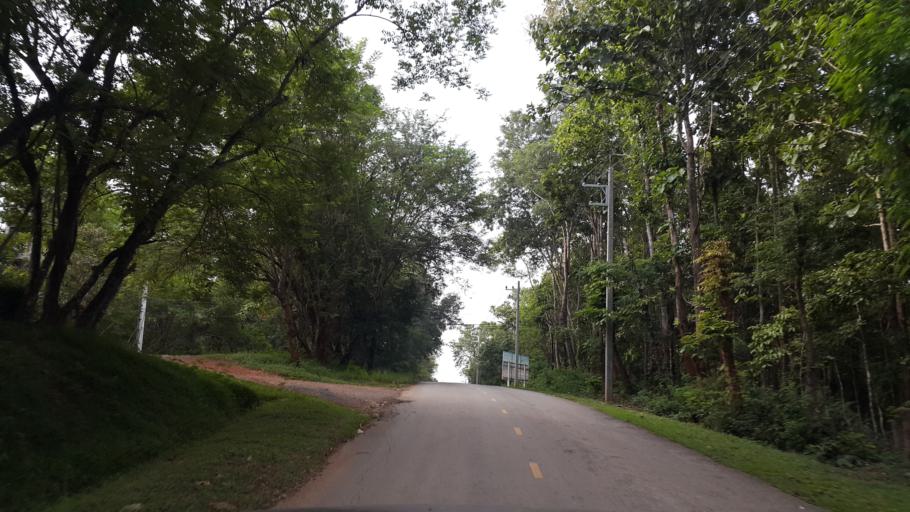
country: TH
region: Chiang Mai
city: Mae On
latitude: 18.8887
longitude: 99.2224
